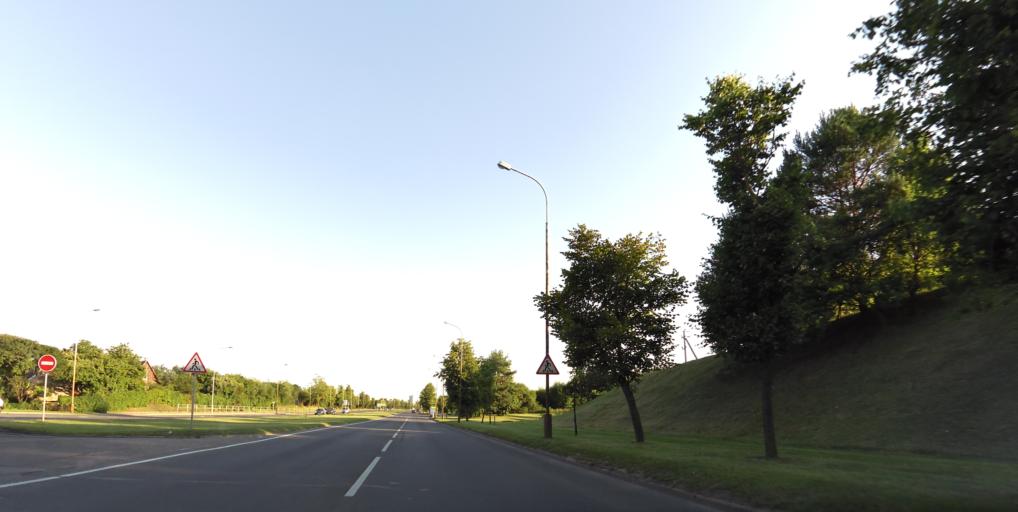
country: LT
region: Vilnius County
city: Seskine
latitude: 54.7223
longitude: 25.2698
